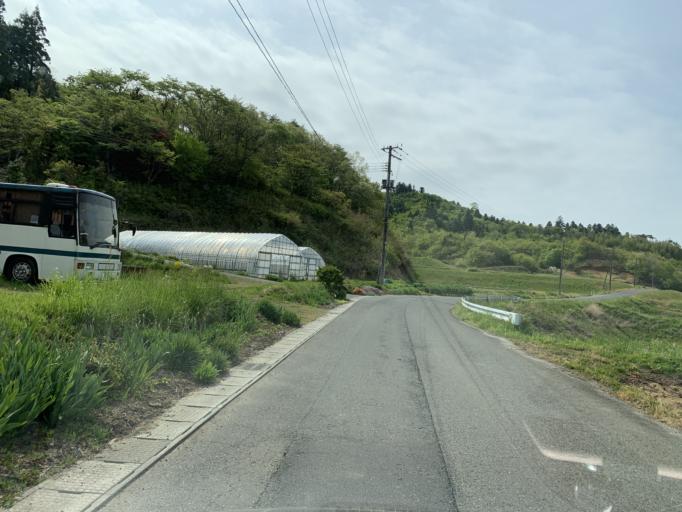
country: JP
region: Iwate
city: Ichinoseki
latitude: 38.8975
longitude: 141.0612
